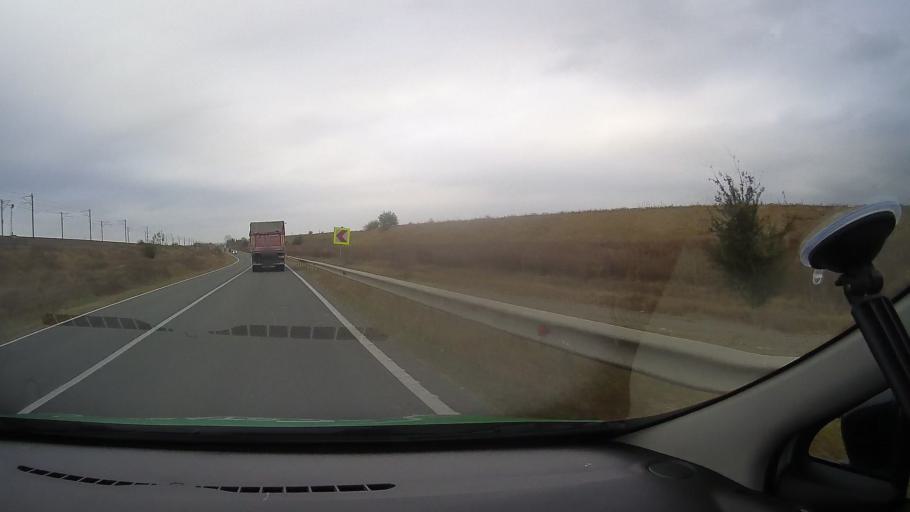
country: RO
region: Constanta
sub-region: Comuna Poarta Alba
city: Poarta Alba
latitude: 44.2216
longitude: 28.3872
